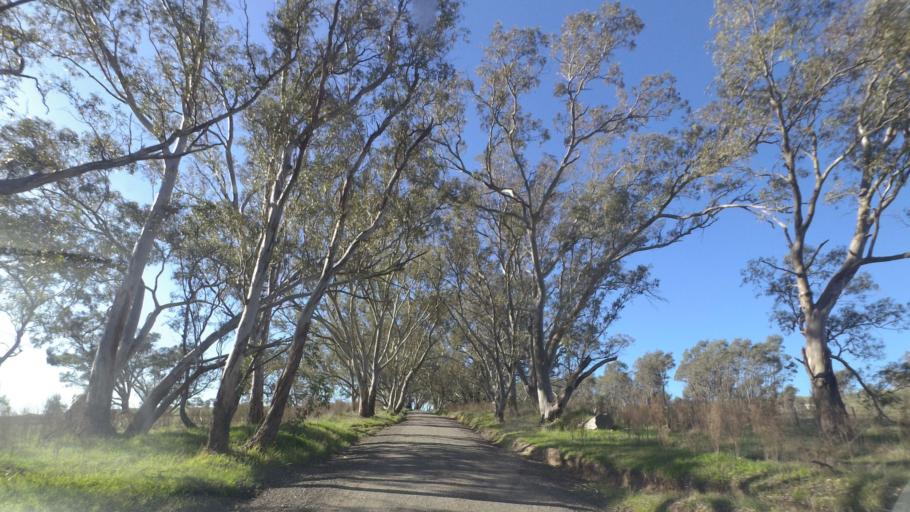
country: AU
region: Victoria
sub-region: Mount Alexander
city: Castlemaine
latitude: -36.9629
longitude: 144.3296
